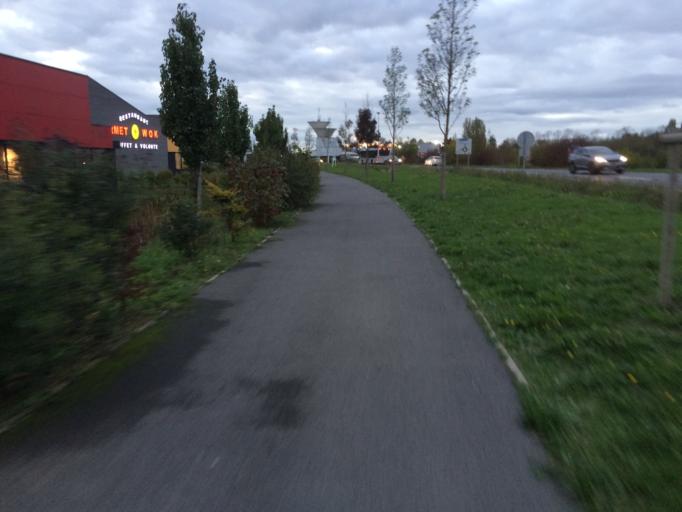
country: FR
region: Ile-de-France
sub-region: Departement de l'Essonne
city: Villejust
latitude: 48.6852
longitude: 2.2208
